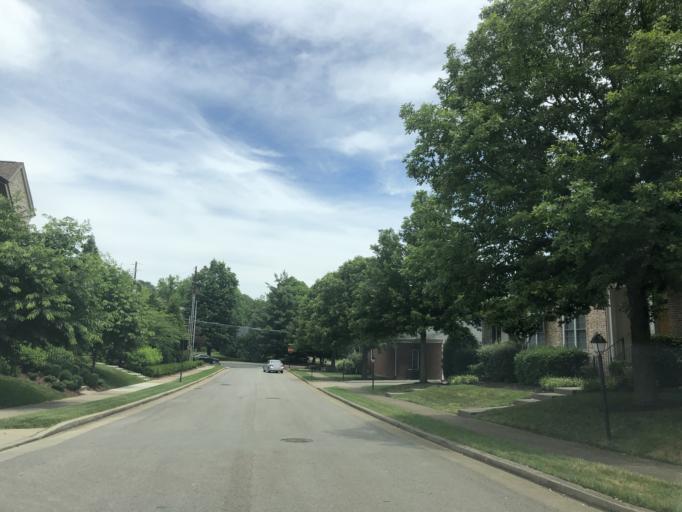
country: US
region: Tennessee
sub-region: Davidson County
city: Oak Hill
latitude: 36.1070
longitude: -86.8048
